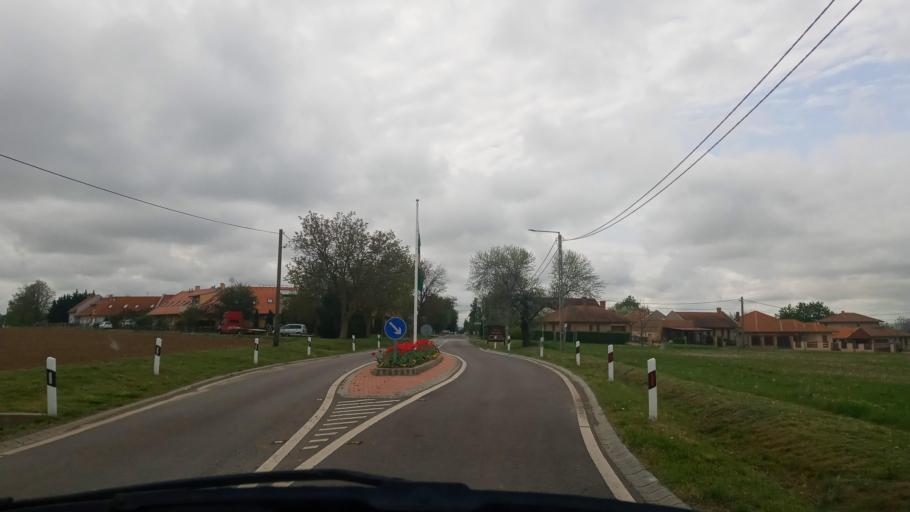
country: HU
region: Baranya
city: Kozarmisleny
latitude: 46.0068
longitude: 18.3743
